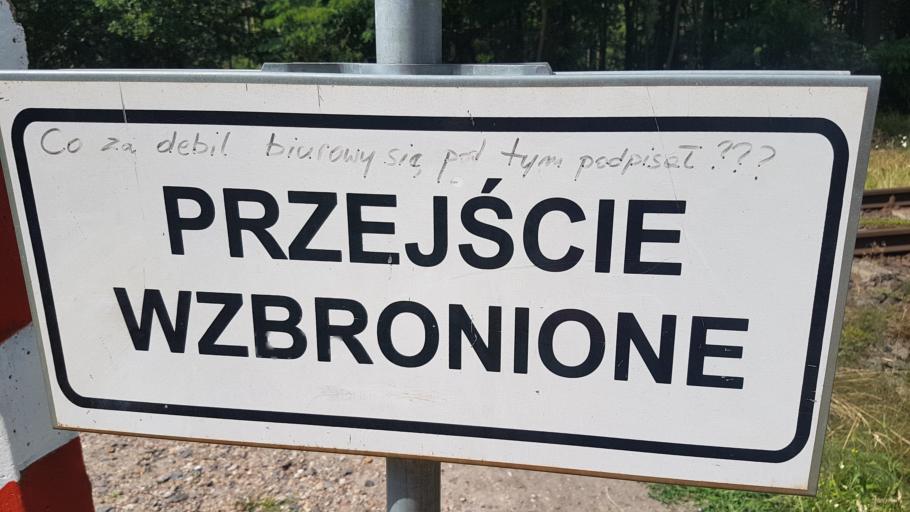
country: PL
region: Lubusz
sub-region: Zielona Gora
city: Zielona Gora
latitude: 51.9456
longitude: 15.4658
